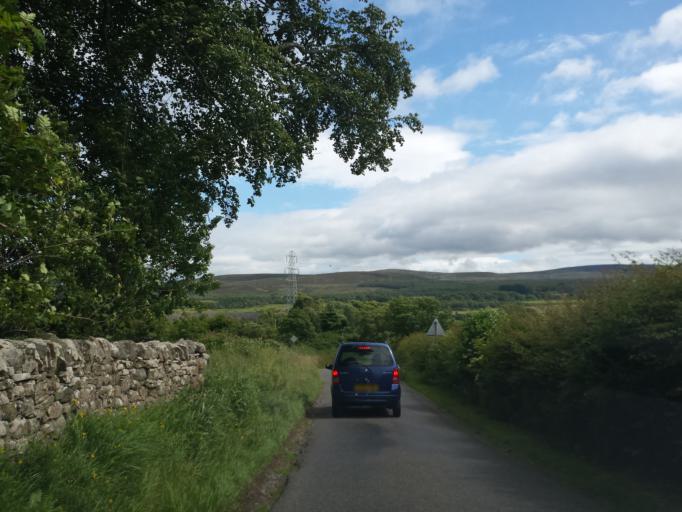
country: GB
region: Scotland
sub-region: Highland
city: Fortrose
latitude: 57.4771
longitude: -4.0780
